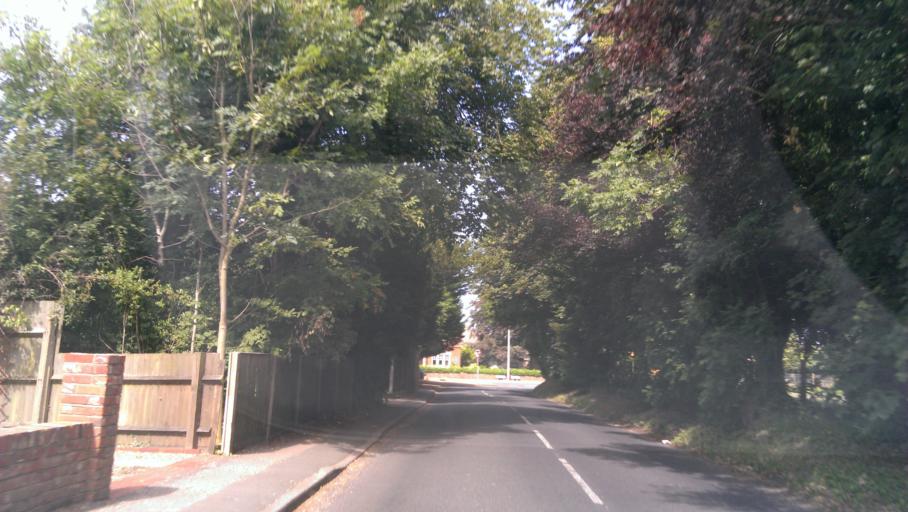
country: GB
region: England
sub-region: Kent
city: Faversham
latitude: 51.3091
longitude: 0.8807
